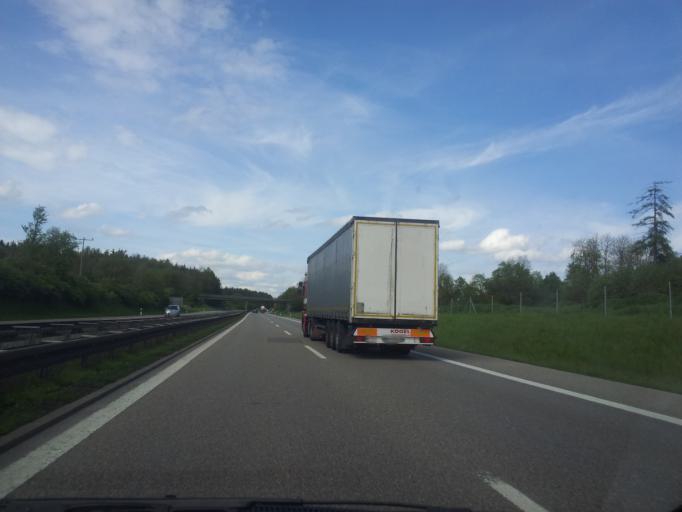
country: DE
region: Baden-Wuerttemberg
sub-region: Tuebingen Region
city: Aitrach
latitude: 47.9511
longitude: 10.1055
